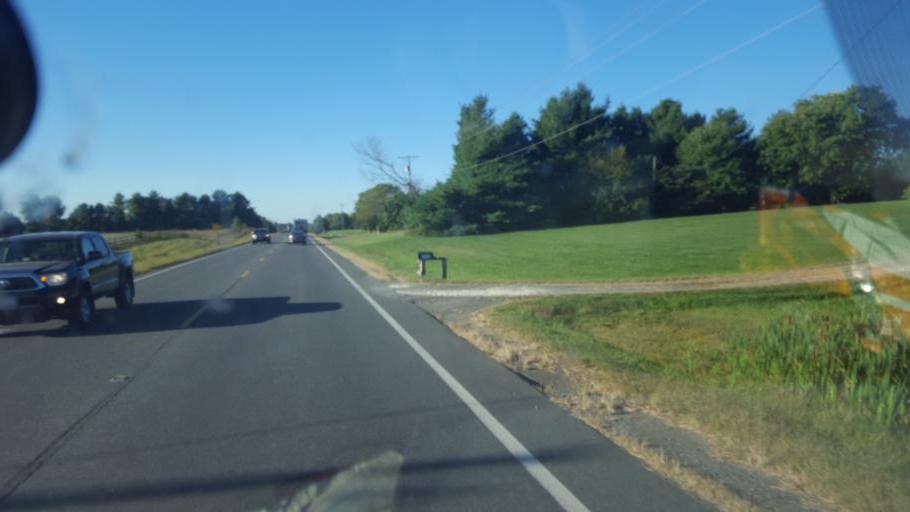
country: US
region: Virginia
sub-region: Prince William County
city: Nokesville
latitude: 38.6814
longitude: -77.6245
